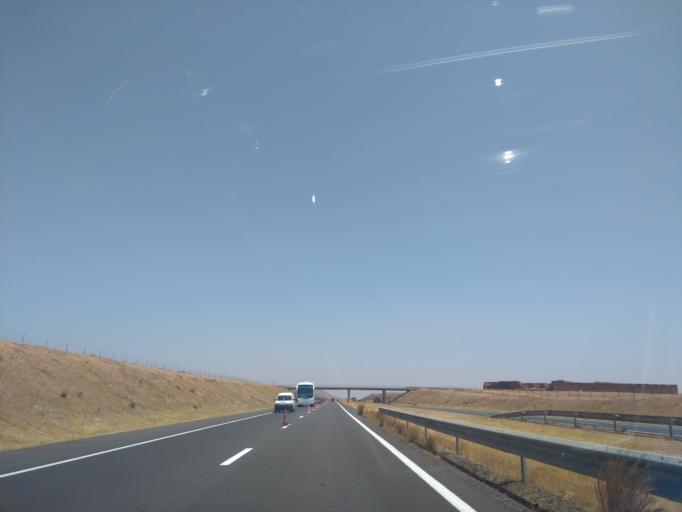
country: MA
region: Marrakech-Tensift-Al Haouz
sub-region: Kelaa-Des-Sraghna
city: Sidi Abdallah
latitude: 32.4350
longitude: -7.9315
